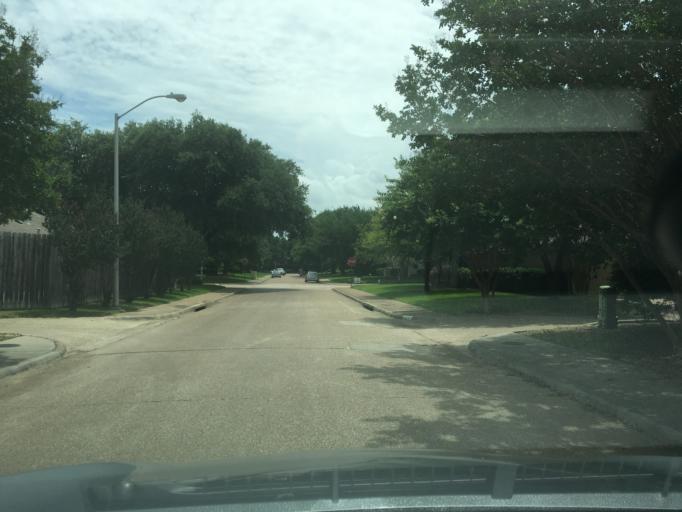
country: US
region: Texas
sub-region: Dallas County
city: Richardson
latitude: 32.9265
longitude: -96.7169
